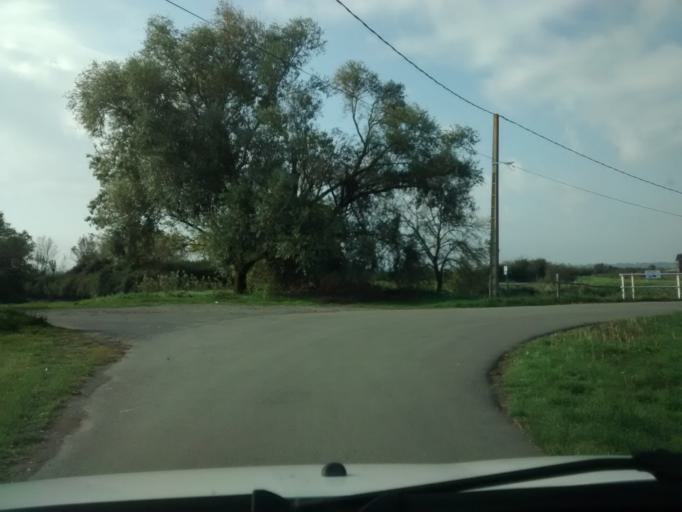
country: FR
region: Pays de la Loire
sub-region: Departement de la Loire-Atlantique
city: Vue
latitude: 47.2382
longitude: -1.8719
